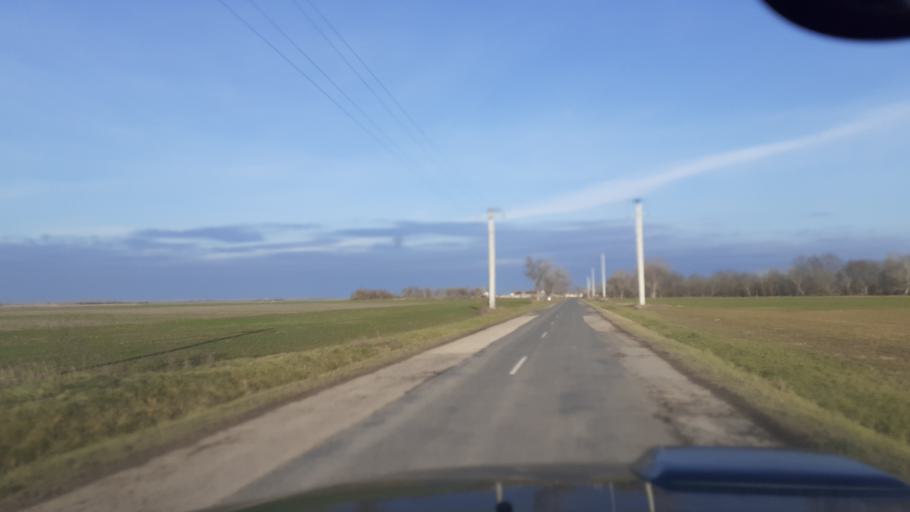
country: HU
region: Pest
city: Domsod
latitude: 47.1054
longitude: 19.0516
